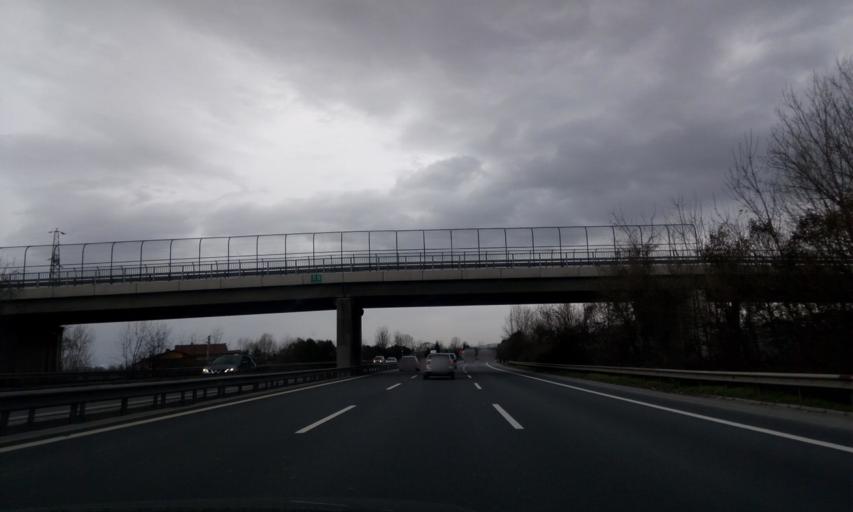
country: TR
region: Kocaeli
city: Derbent
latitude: 40.7133
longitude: 30.1182
